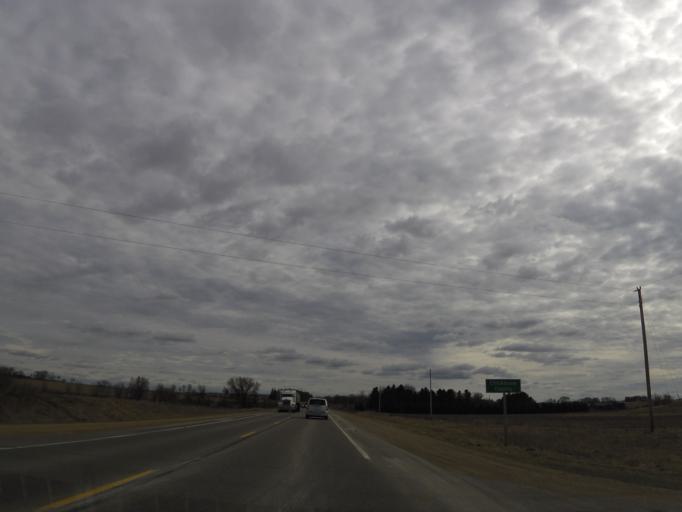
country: US
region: Iowa
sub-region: Chickasaw County
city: New Hampton
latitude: 43.2127
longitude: -92.2982
